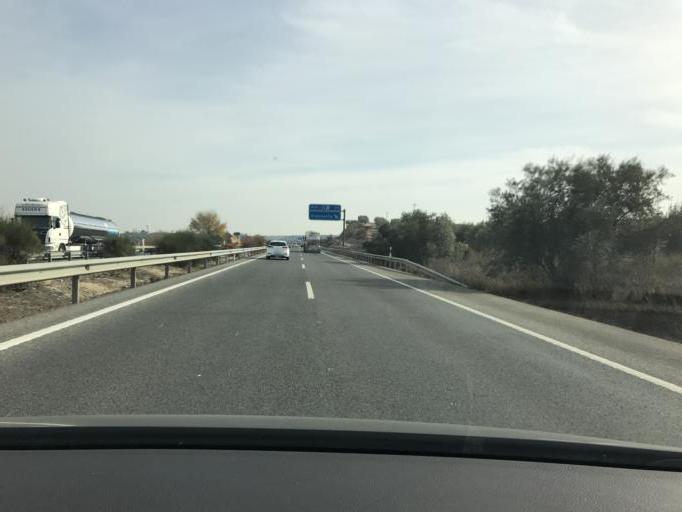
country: ES
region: Andalusia
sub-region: Provincia de Granada
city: Moraleda de Zafayona
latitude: 37.1799
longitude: -3.9177
